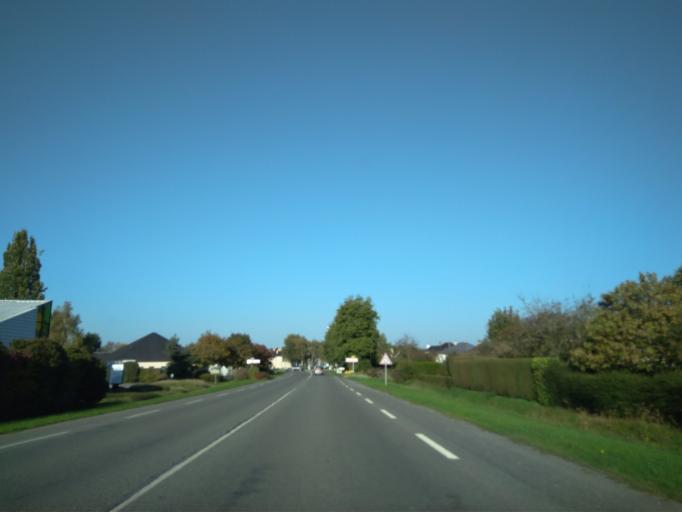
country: FR
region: Pays de la Loire
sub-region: Departement de la Mayenne
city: Louverne
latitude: 48.1185
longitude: -0.7248
